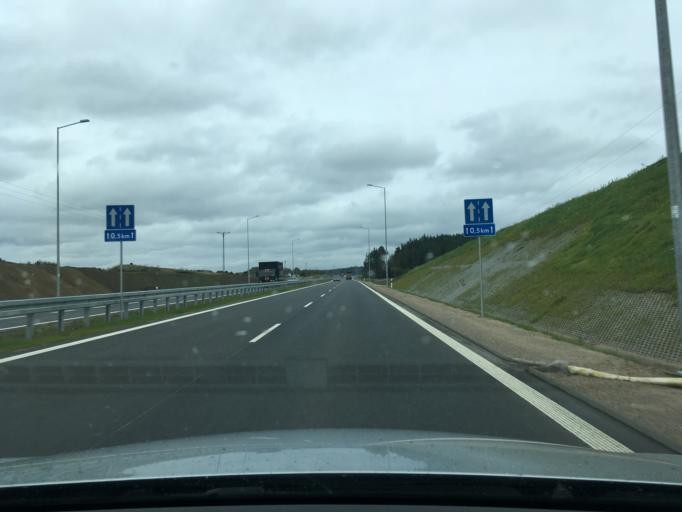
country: PL
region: Pomeranian Voivodeship
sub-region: Powiat koscierski
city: Koscierzyna
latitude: 54.1087
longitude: 17.9809
